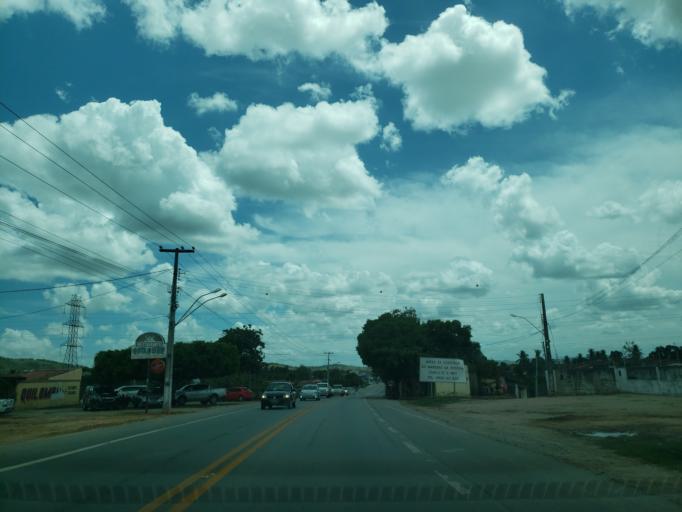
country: BR
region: Alagoas
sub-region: Uniao Dos Palmares
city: Uniao dos Palmares
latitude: -9.1585
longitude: -36.0144
